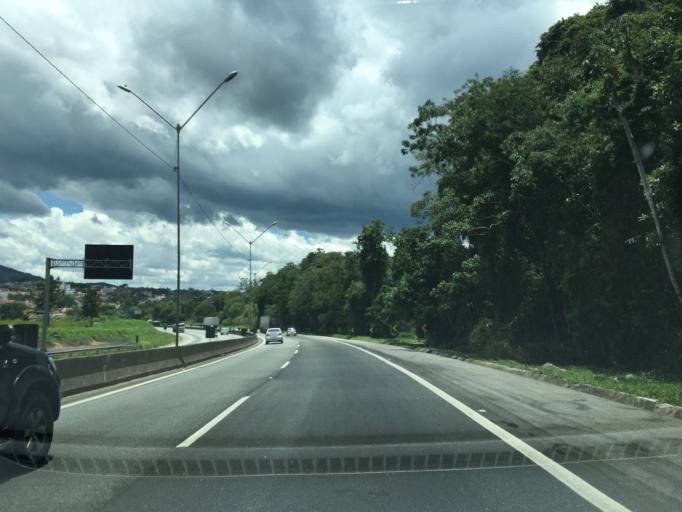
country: BR
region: Sao Paulo
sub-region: Mairipora
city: Mairipora
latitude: -23.3095
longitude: -46.5804
